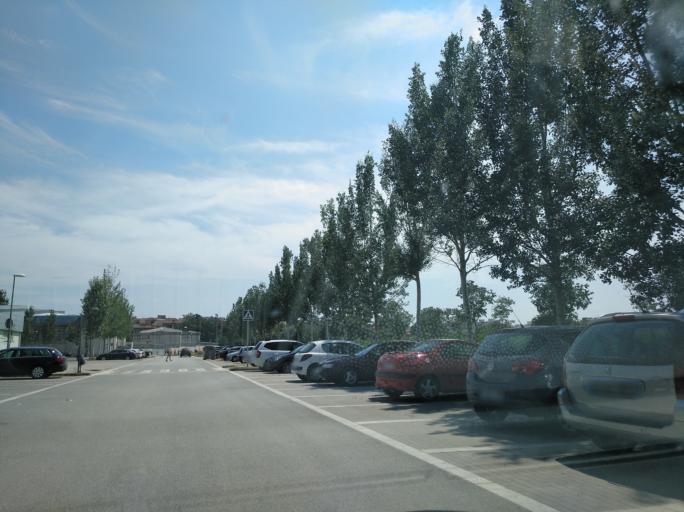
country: ES
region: Catalonia
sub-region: Provincia de Girona
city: Girona
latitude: 41.9823
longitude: 2.8091
